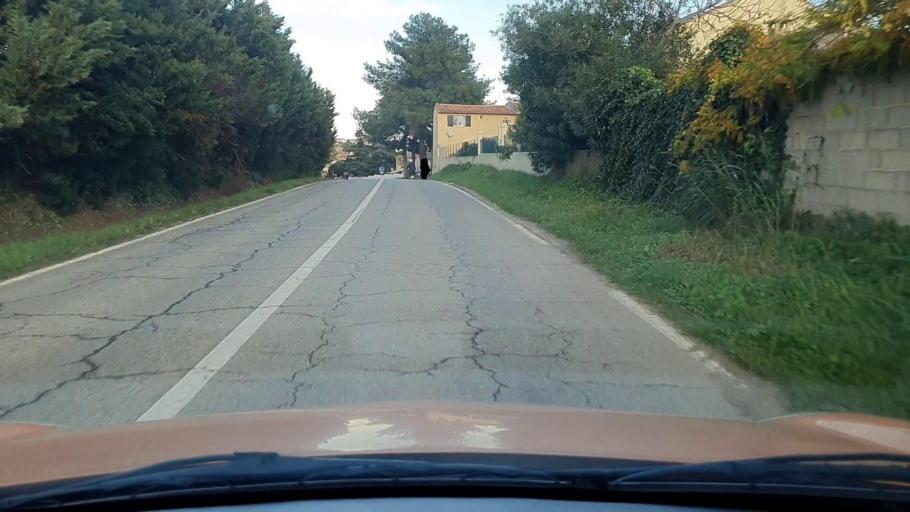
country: FR
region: Languedoc-Roussillon
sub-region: Departement du Gard
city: Saint-Gilles
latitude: 43.6739
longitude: 4.4237
